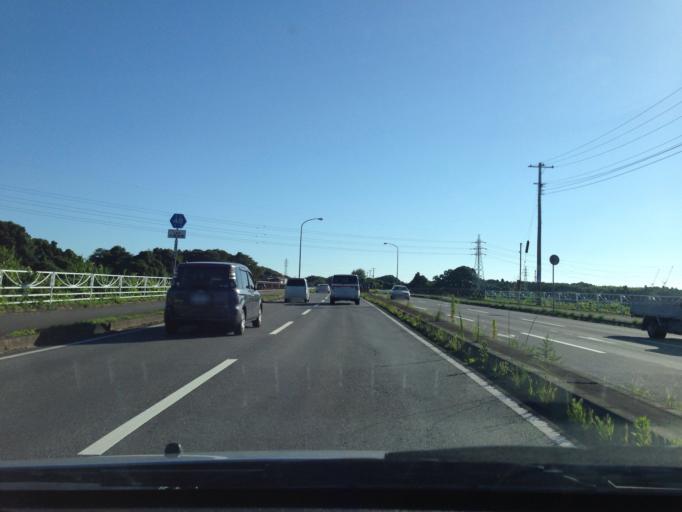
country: JP
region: Ibaraki
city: Ami
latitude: 36.0554
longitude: 140.1931
